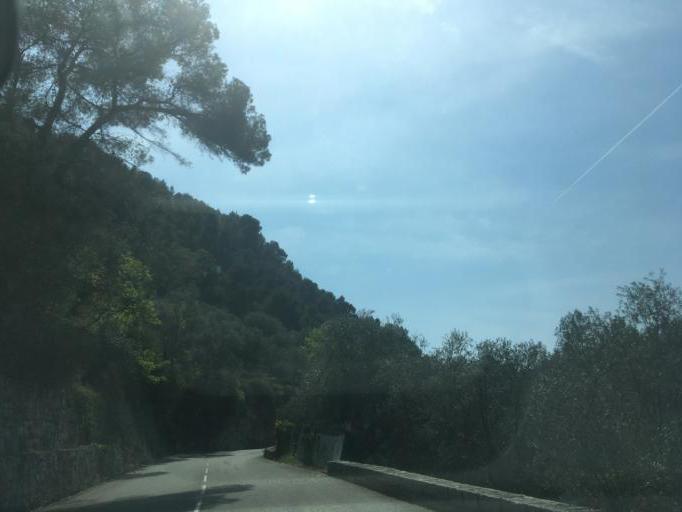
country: FR
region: Provence-Alpes-Cote d'Azur
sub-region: Departement des Alpes-Maritimes
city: Saint-Martin-du-Var
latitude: 43.8290
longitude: 7.1936
